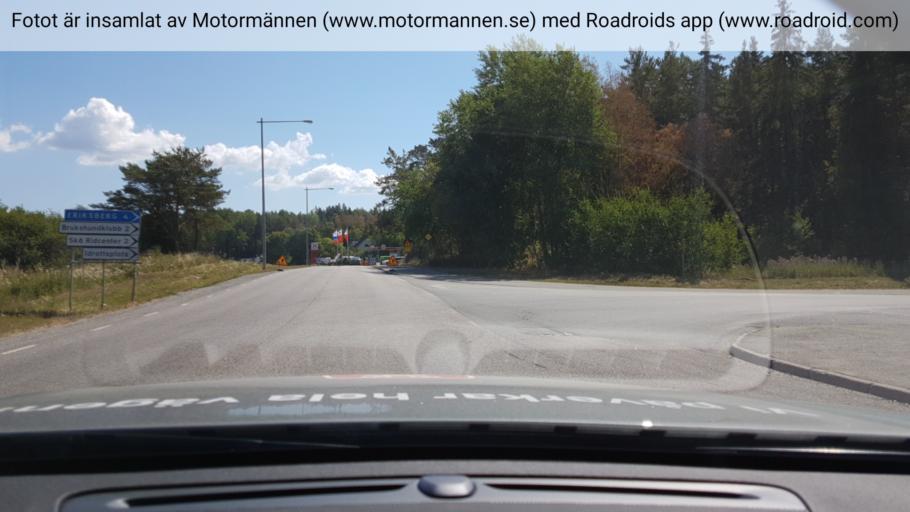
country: SE
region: Stockholm
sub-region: Ekero Kommun
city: Ekeroe
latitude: 59.3247
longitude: 17.7478
